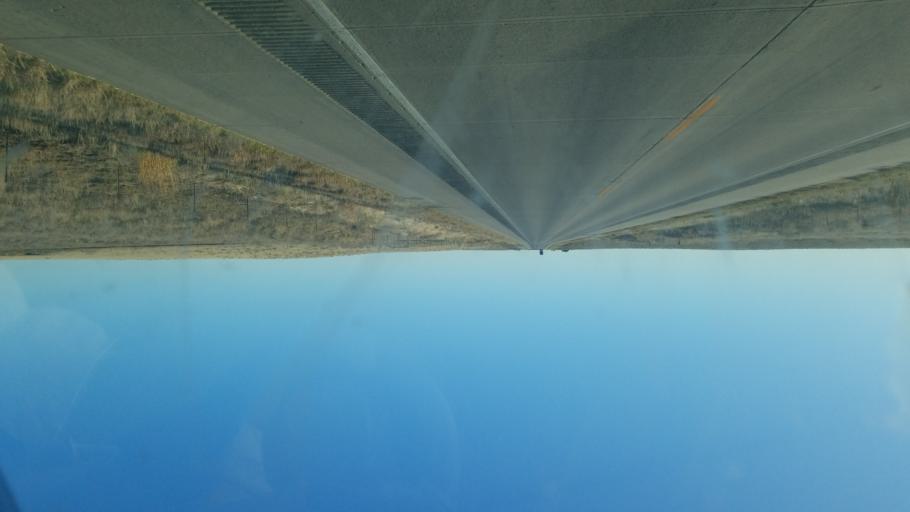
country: US
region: Colorado
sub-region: Kiowa County
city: Eads
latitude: 38.6014
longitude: -102.7860
